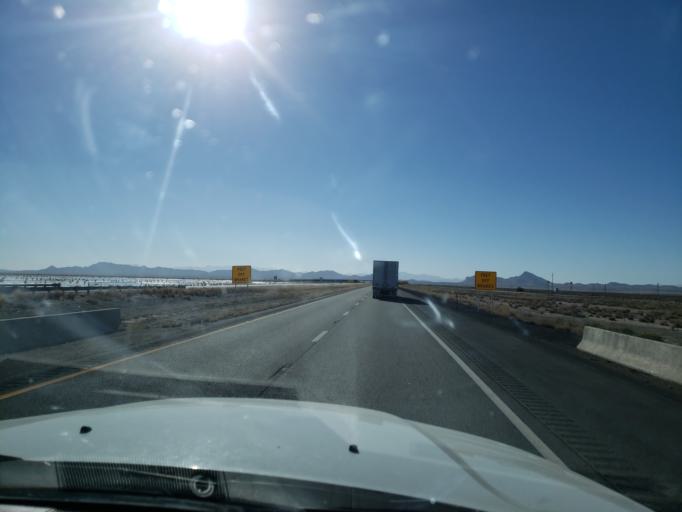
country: US
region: New Mexico
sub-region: Hidalgo County
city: Lordsburg
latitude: 32.2865
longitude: -108.8697
